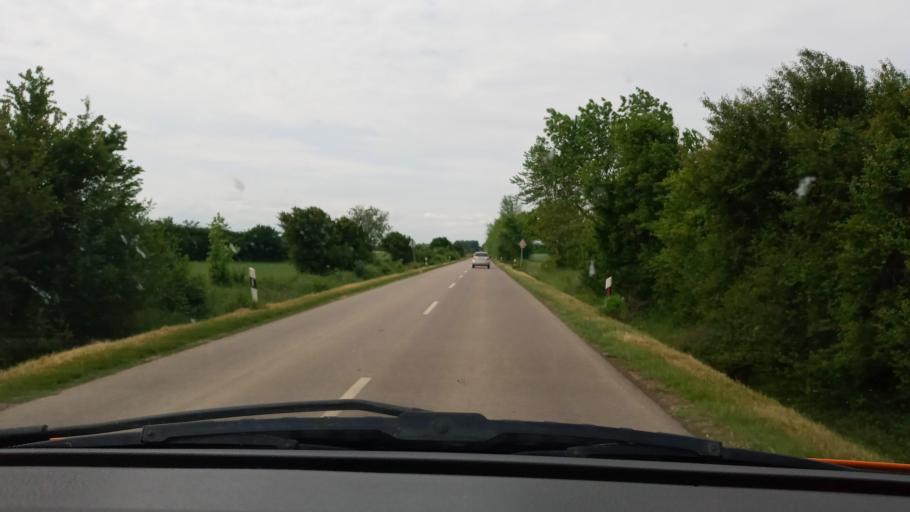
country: HU
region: Baranya
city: Vajszlo
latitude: 45.9174
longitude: 18.0553
